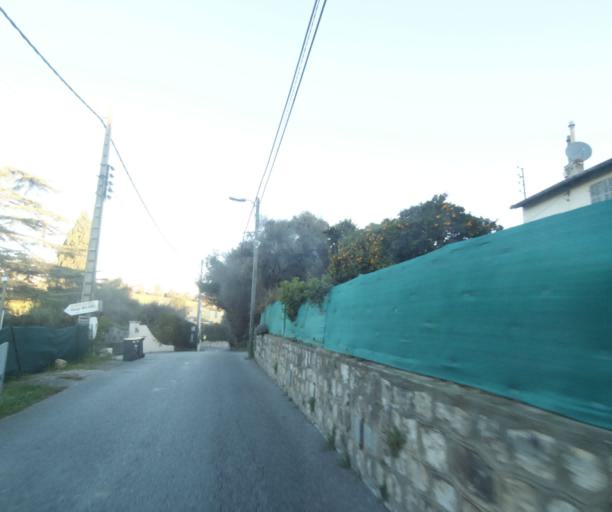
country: FR
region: Provence-Alpes-Cote d'Azur
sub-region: Departement des Alpes-Maritimes
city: Vallauris
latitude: 43.5855
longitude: 7.0812
